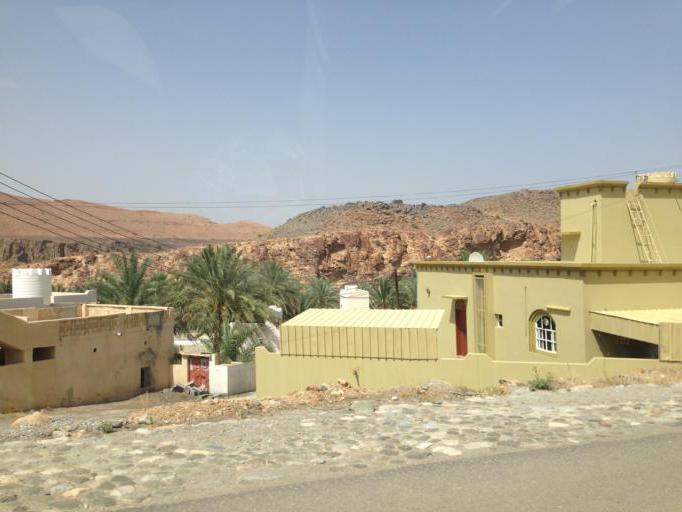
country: OM
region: Ash Sharqiyah
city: Ibra'
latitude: 23.0816
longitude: 58.8683
